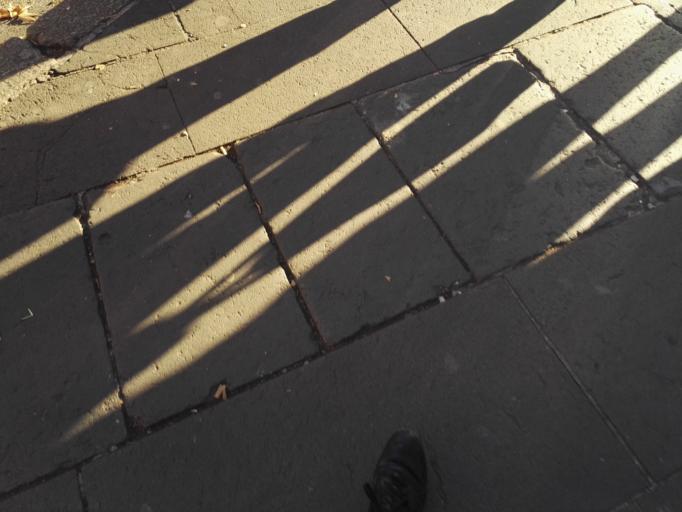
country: IT
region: Latium
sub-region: Citta metropolitana di Roma Capitale
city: Rome
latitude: 41.9041
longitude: 12.4886
